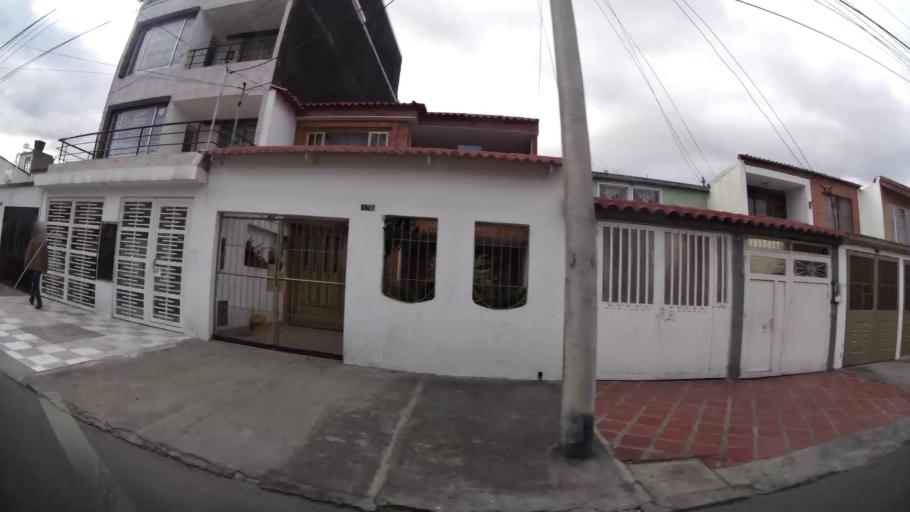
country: CO
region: Bogota D.C.
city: Bogota
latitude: 4.6107
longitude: -74.1178
